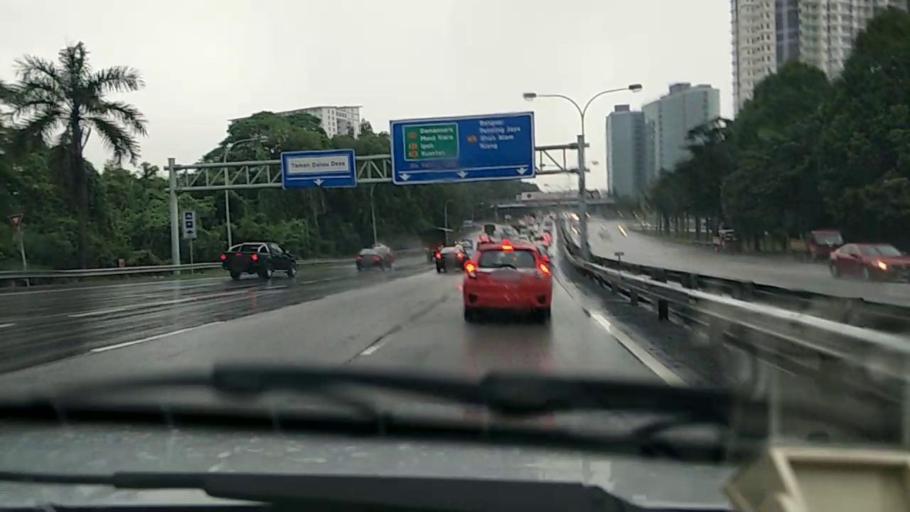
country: MY
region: Kuala Lumpur
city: Kuala Lumpur
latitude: 3.1029
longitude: 101.6952
